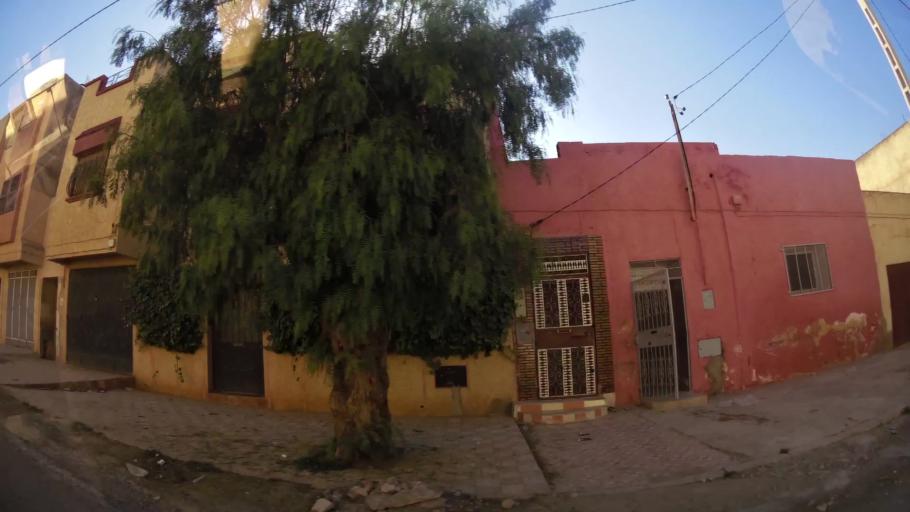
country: MA
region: Oriental
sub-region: Berkane-Taourirt
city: Ahfir
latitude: 34.9558
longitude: -2.0994
